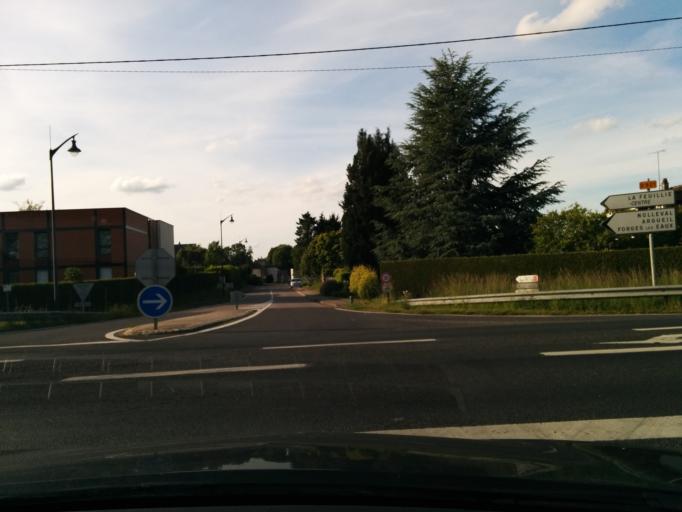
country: FR
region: Haute-Normandie
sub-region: Departement de la Seine-Maritime
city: La Feuillie
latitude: 49.4596
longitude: 1.5143
